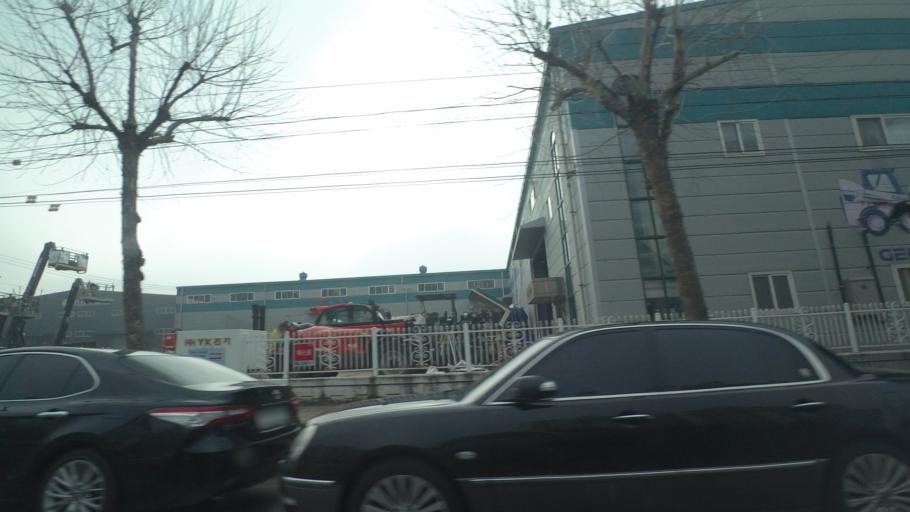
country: KR
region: Gyeonggi-do
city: Hwaseong-si
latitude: 36.9874
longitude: 126.8508
